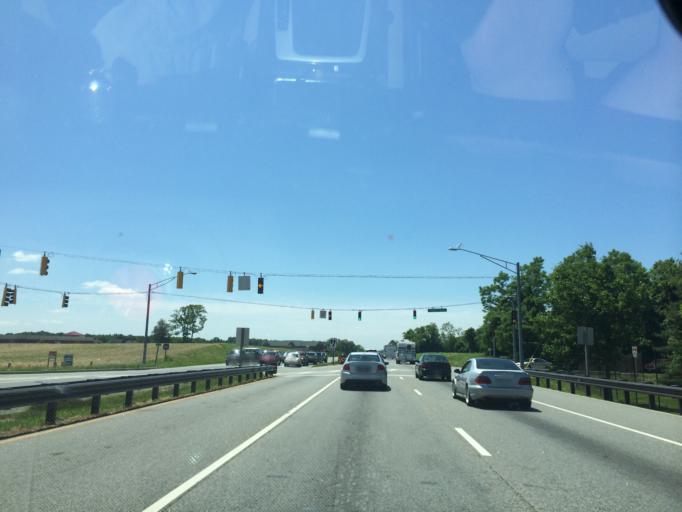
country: US
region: Maryland
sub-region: Talbot County
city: Easton
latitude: 38.7936
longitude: -76.0602
